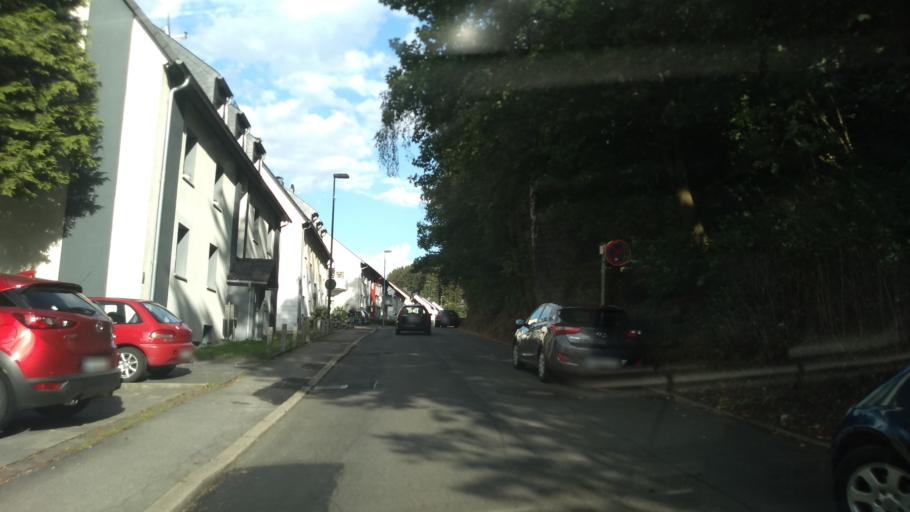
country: DE
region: North Rhine-Westphalia
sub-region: Regierungsbezirk Arnsberg
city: Schalksmuhle
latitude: 51.2127
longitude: 7.5735
